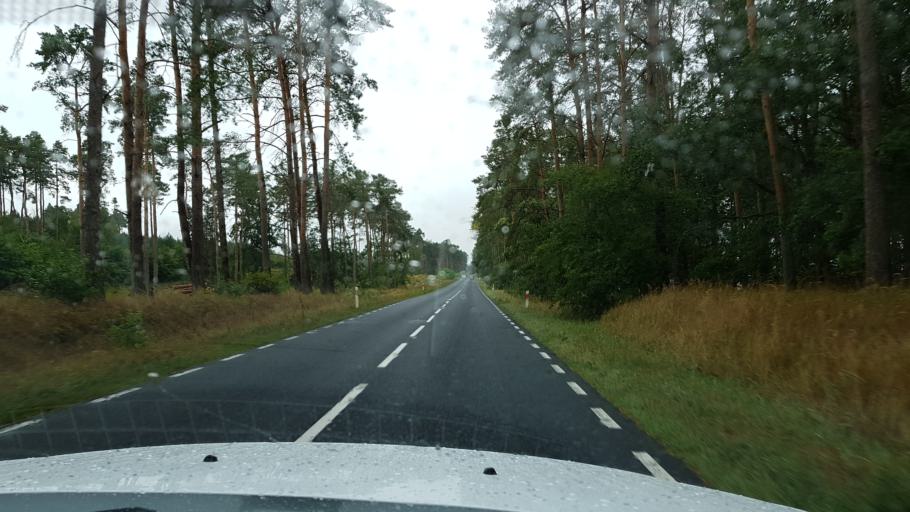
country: DE
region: Brandenburg
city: Schwedt (Oder)
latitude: 53.0486
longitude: 14.3427
